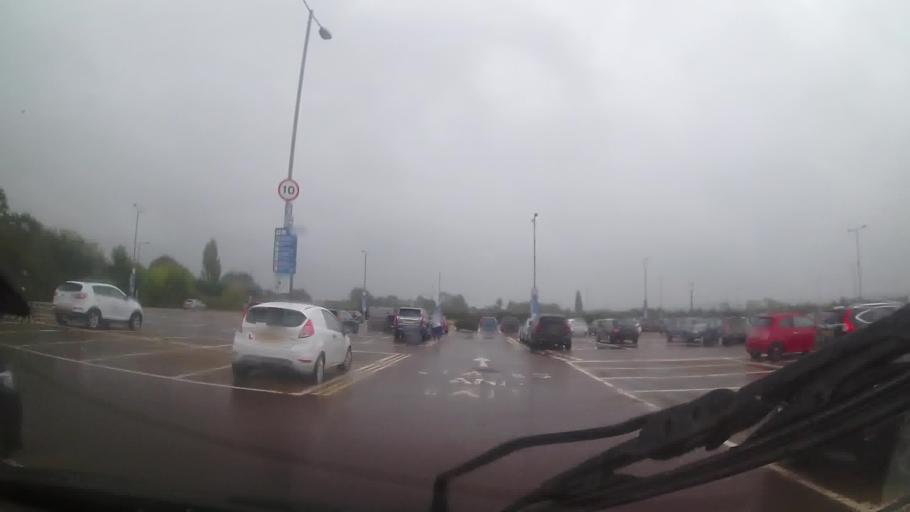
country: GB
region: England
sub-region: Oxfordshire
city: Kidlington
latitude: 51.7934
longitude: -1.2815
